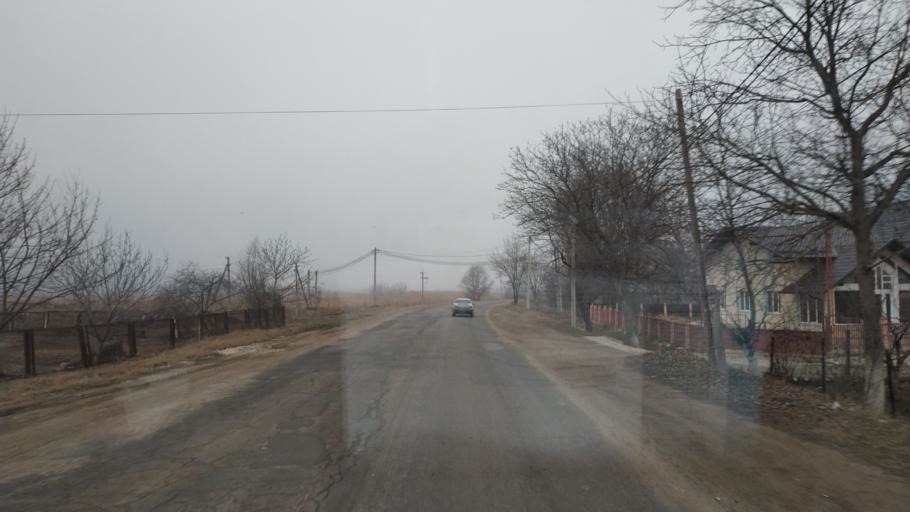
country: MD
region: Laloveni
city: Ialoveni
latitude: 46.9449
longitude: 28.7740
